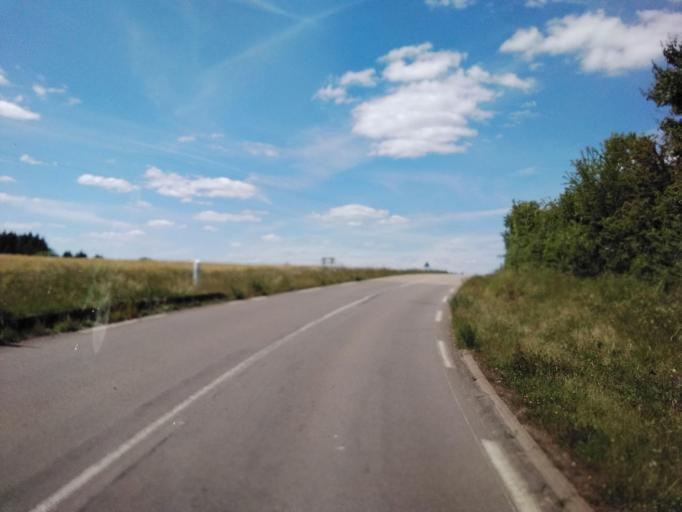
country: FR
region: Bourgogne
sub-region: Departement de l'Yonne
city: Joux-la-Ville
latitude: 47.5675
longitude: 3.8854
